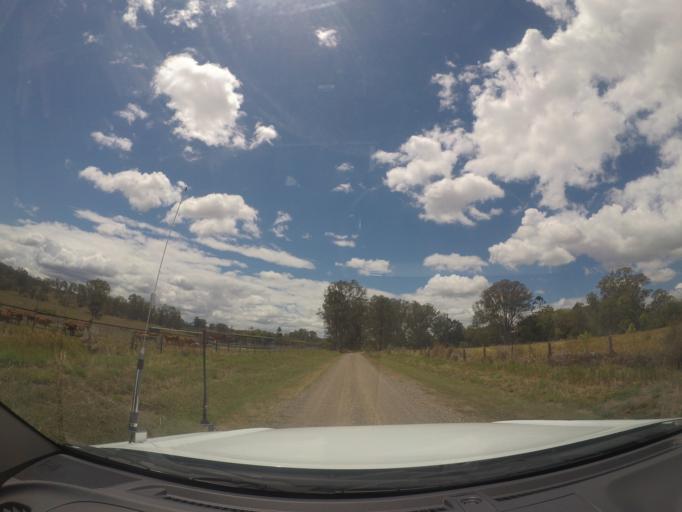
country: AU
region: Queensland
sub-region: Logan
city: Cedar Vale
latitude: -27.9001
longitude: 153.0625
